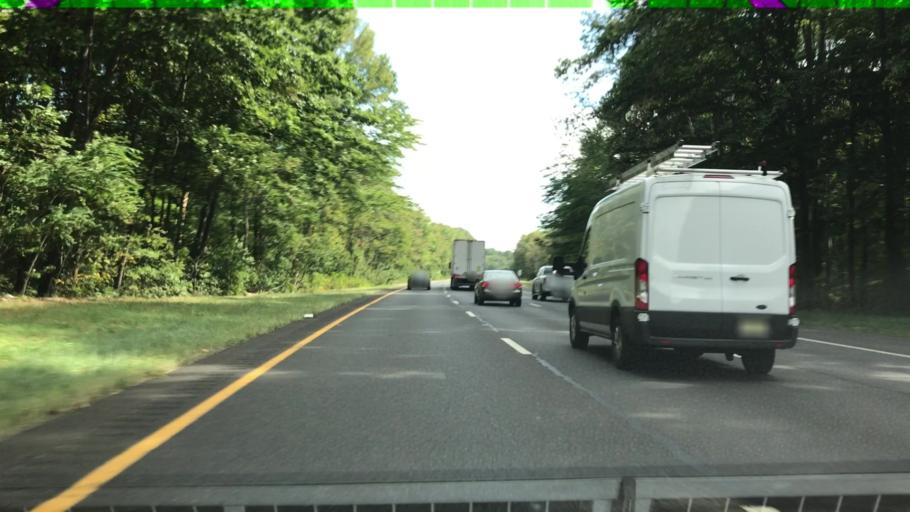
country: US
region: New Jersey
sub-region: Burlington County
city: Burlington
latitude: 40.0618
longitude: -74.8084
